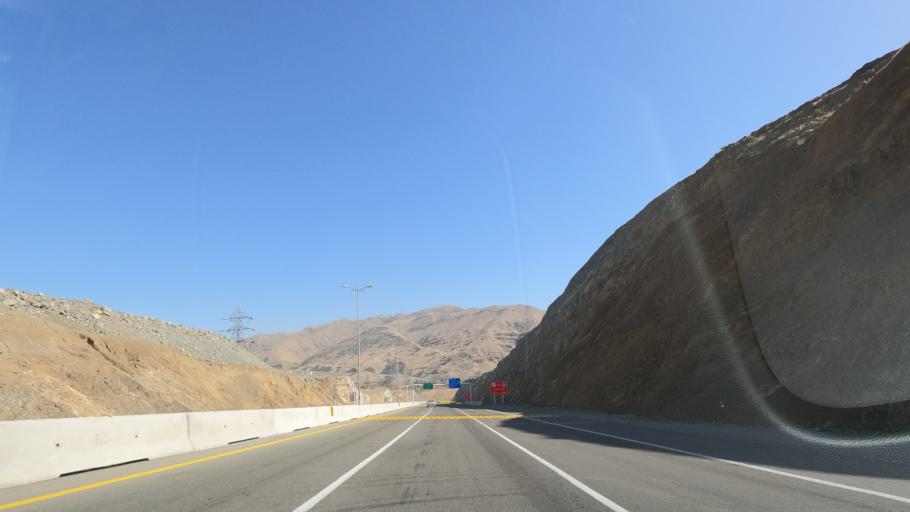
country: IR
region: Alborz
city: Karaj
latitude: 35.8177
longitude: 51.0379
